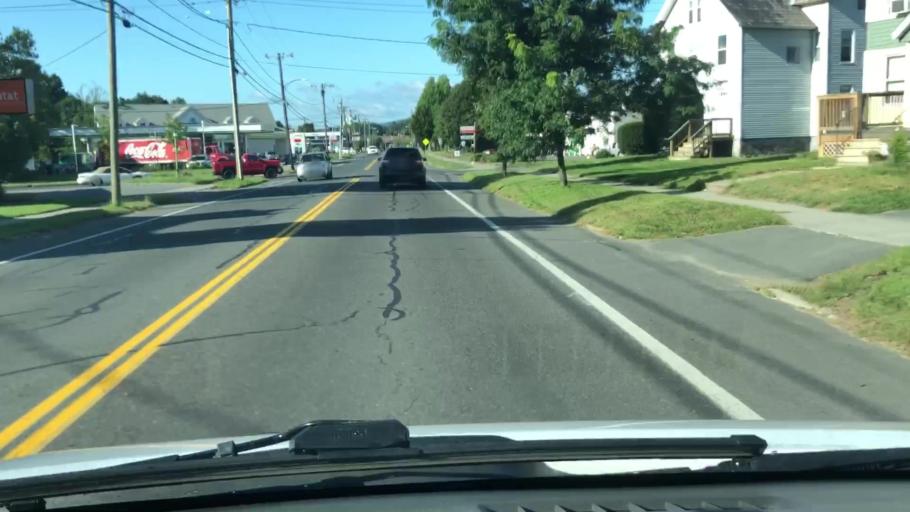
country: US
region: Massachusetts
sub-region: Franklin County
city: Greenfield
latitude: 42.6023
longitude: -72.5926
